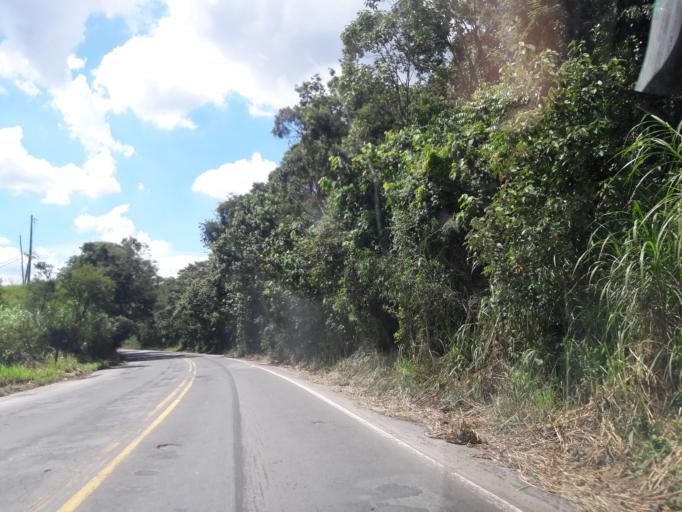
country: BR
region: Sao Paulo
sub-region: Campo Limpo Paulista
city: Campo Limpo Paulista
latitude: -23.2258
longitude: -46.7882
